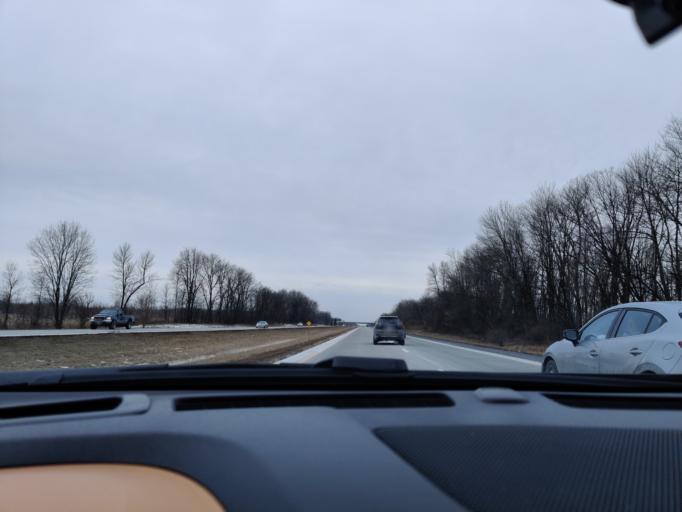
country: US
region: New York
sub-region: St. Lawrence County
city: Massena
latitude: 45.0386
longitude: -74.9294
